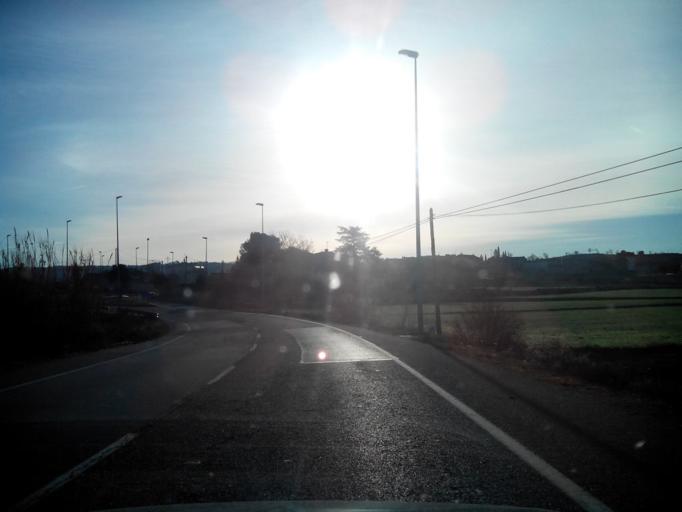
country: ES
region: Catalonia
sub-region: Provincia de Barcelona
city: Sant Fruitos de Bages
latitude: 41.7270
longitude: 1.8595
